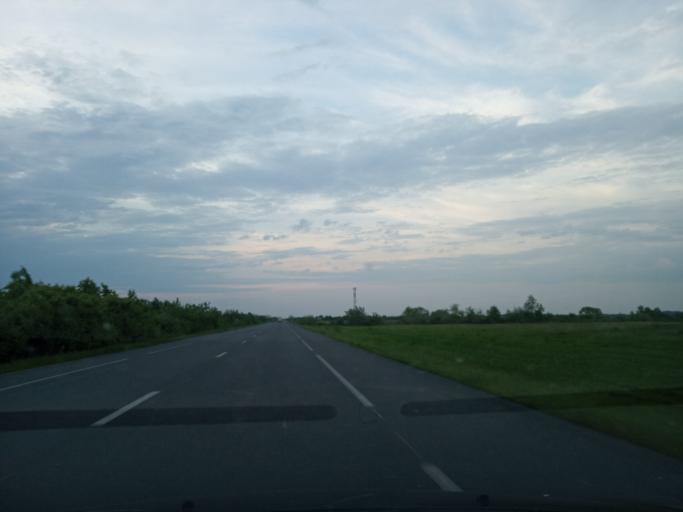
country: RO
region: Timis
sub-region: Oras Deta
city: Deta
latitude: 45.3784
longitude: 21.2330
